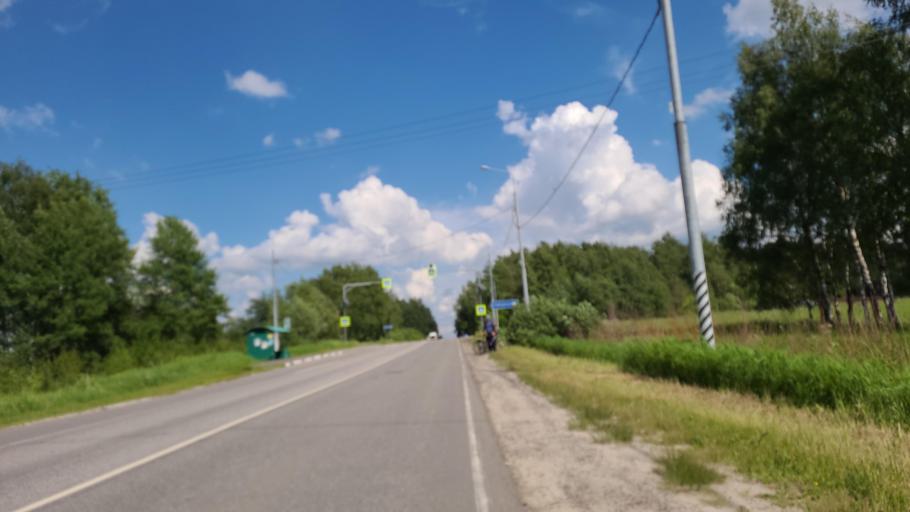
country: RU
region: Moskovskaya
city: Konobeyevo
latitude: 55.4019
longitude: 38.6735
